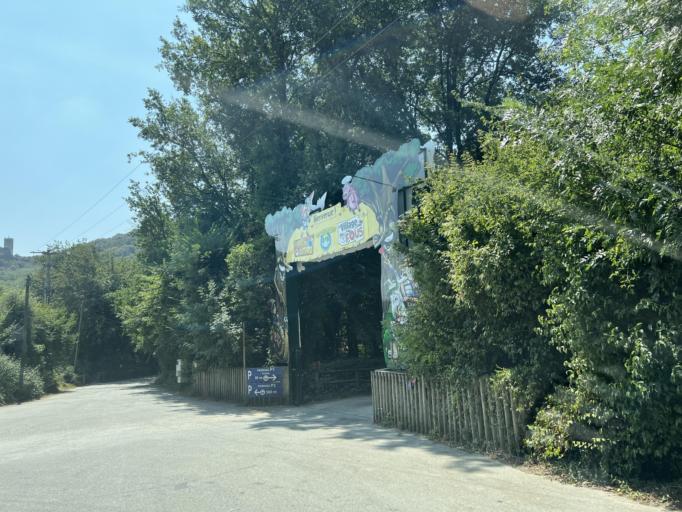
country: FR
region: Provence-Alpes-Cote d'Azur
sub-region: Departement des Alpes-Maritimes
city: Villeneuve-Loubet
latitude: 43.6585
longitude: 7.0929
